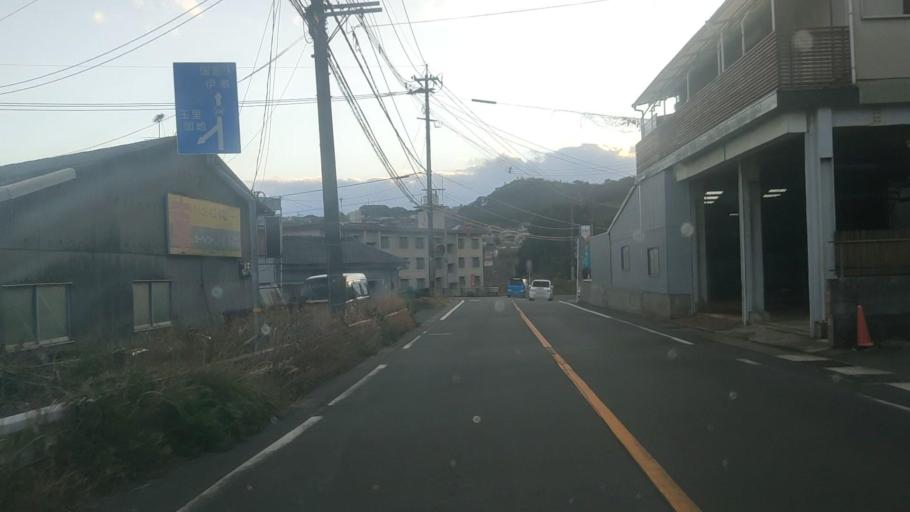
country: JP
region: Kagoshima
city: Kagoshima-shi
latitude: 31.6235
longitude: 130.5425
